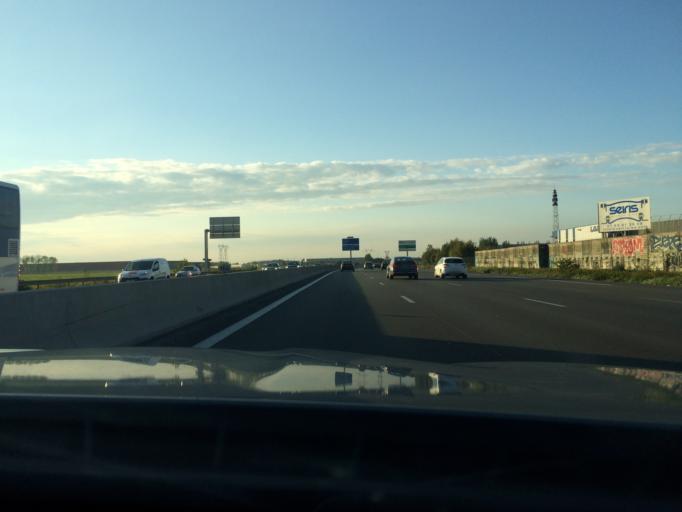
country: FR
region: Ile-de-France
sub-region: Departement de l'Essonne
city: Le Coudray-Montceaux
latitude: 48.5633
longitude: 2.4792
